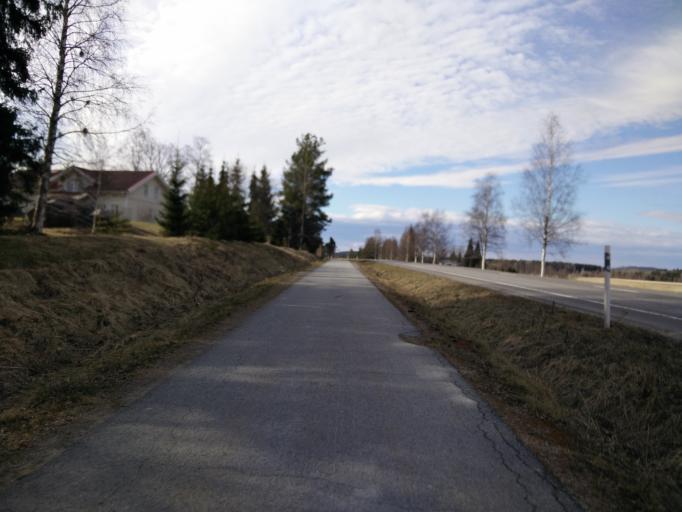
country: FI
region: Pirkanmaa
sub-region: Tampere
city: Orivesi
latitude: 61.7033
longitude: 24.3387
